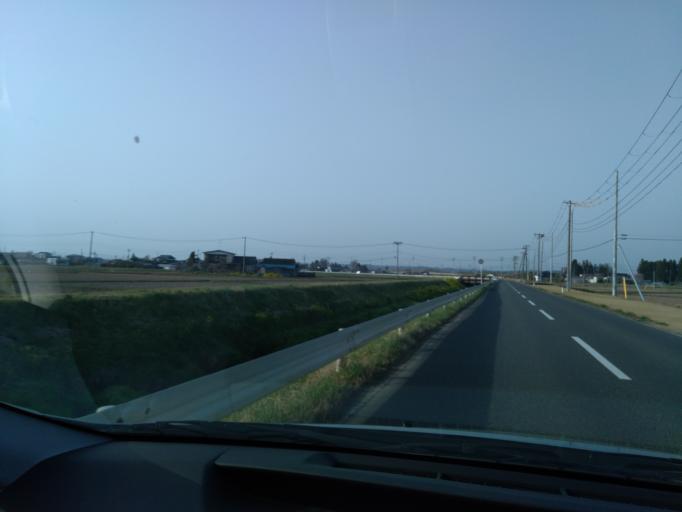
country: JP
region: Iwate
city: Ichinoseki
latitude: 38.7524
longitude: 141.1339
